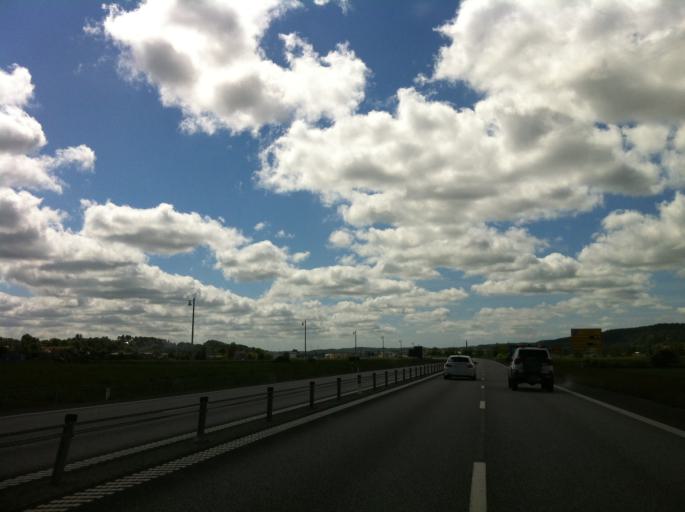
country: SE
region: Vaestra Goetaland
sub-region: Ale Kommun
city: Alvangen
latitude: 57.9655
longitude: 12.1389
